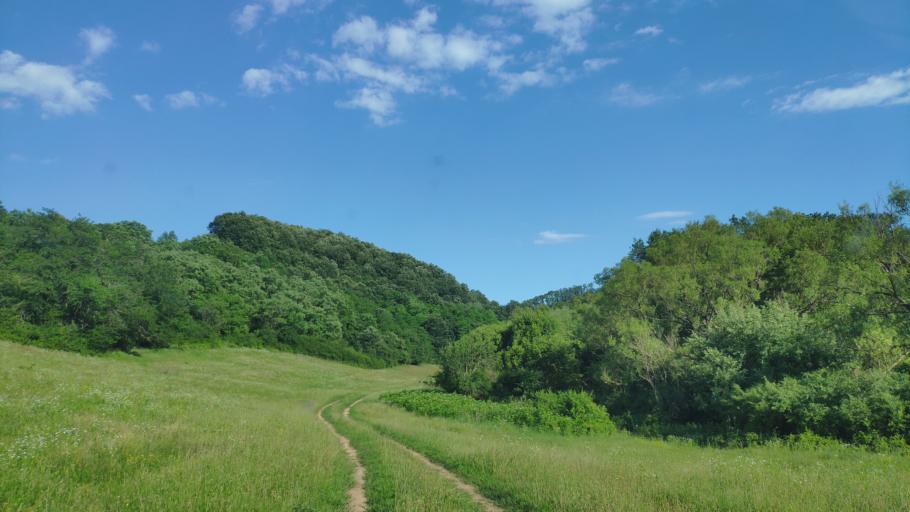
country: SK
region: Banskobystricky
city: Rimavska Sobota
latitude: 48.2458
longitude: 20.1033
